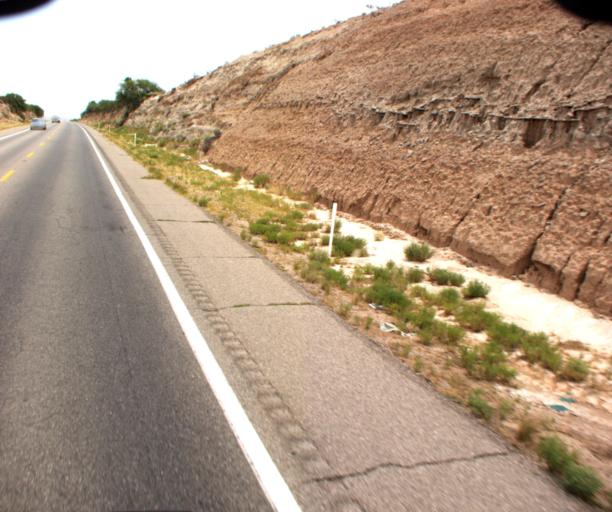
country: US
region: Arizona
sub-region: Graham County
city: Bylas
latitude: 33.0791
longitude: -110.0399
